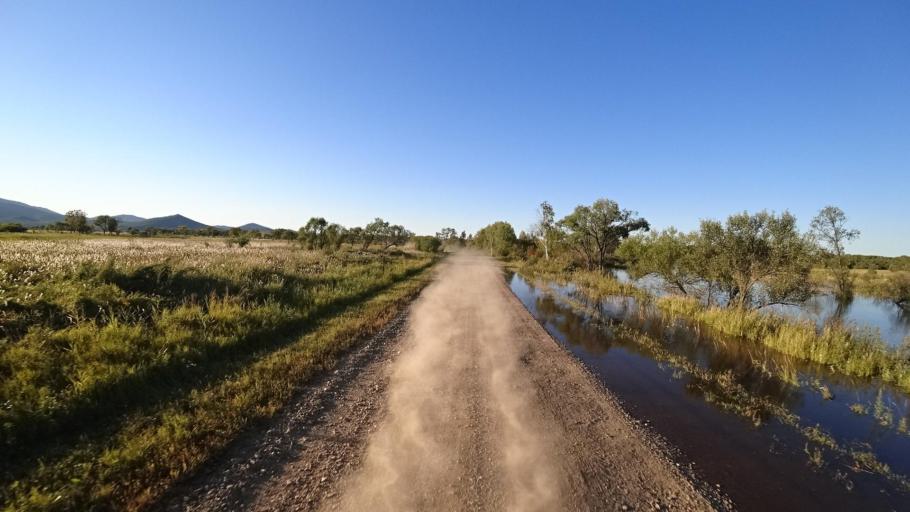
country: RU
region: Primorskiy
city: Kirovskiy
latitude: 44.8117
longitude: 133.6163
